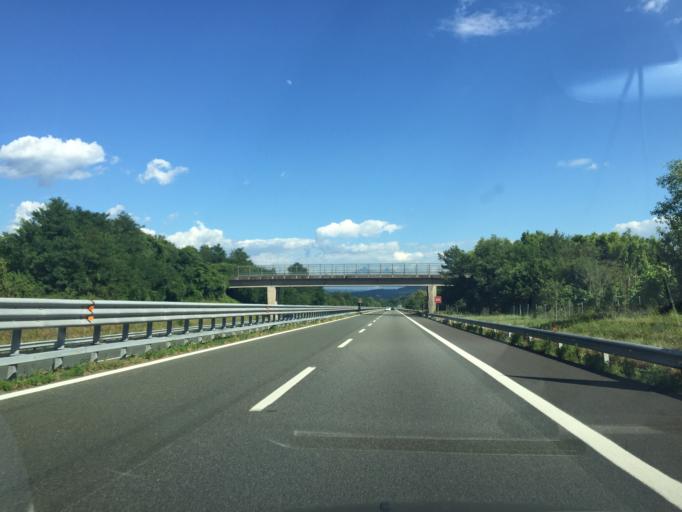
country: IT
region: Tuscany
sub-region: Provincia di Massa-Carrara
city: Filattiera
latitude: 44.3241
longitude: 9.9155
